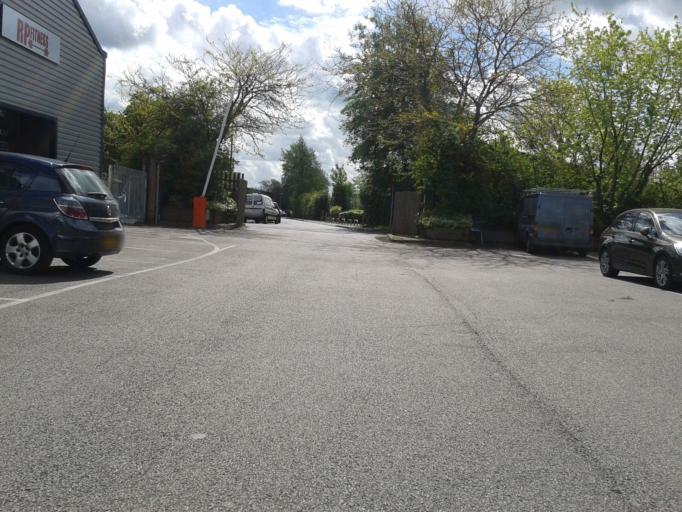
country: GB
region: England
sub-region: Cambridgeshire
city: Cambridge
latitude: 52.2288
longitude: 0.1491
